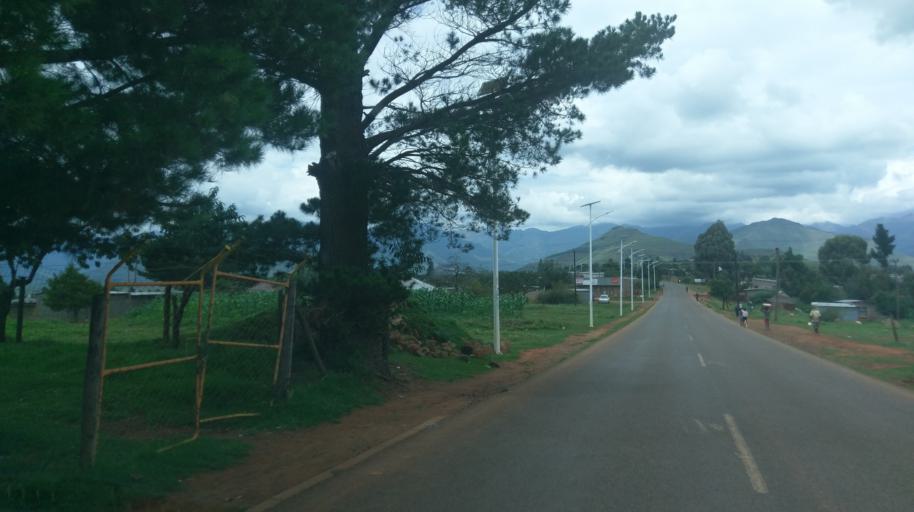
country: LS
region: Leribe
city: Leribe
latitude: -29.0054
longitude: 28.2125
